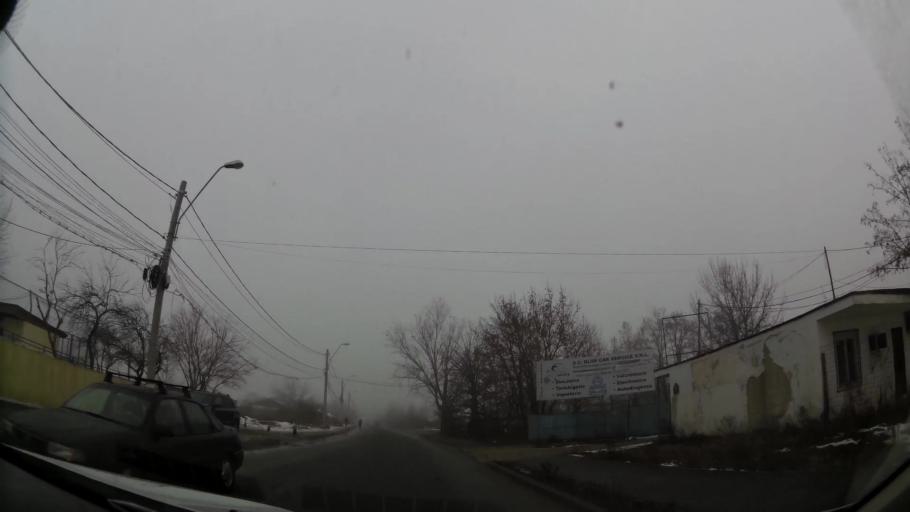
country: RO
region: Ilfov
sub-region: Comuna Chiajna
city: Rosu
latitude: 44.4736
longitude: 26.0165
